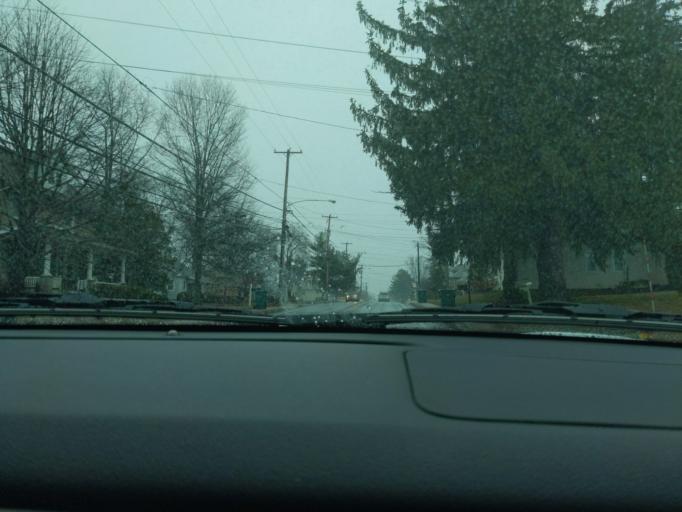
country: US
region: Pennsylvania
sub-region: Bucks County
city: Dublin
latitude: 40.3693
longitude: -75.1991
